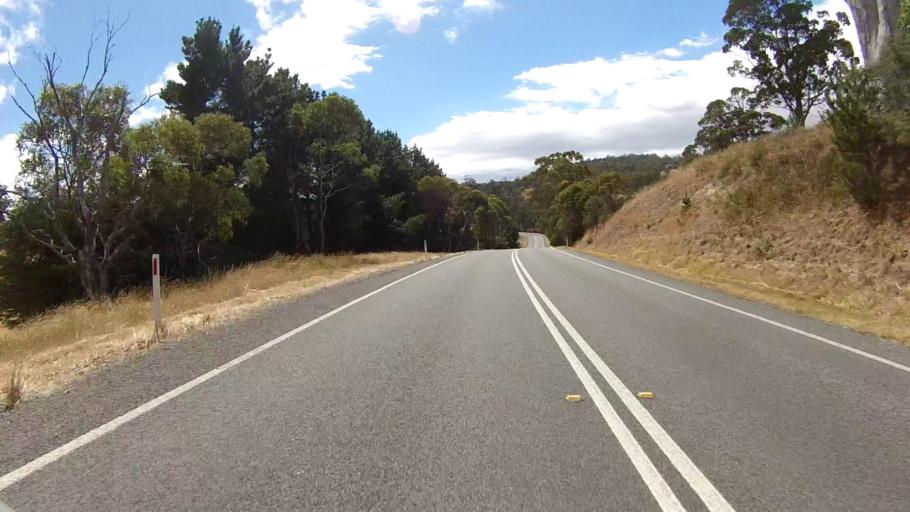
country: AU
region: Tasmania
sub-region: Sorell
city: Sorell
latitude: -42.6286
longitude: 147.6291
